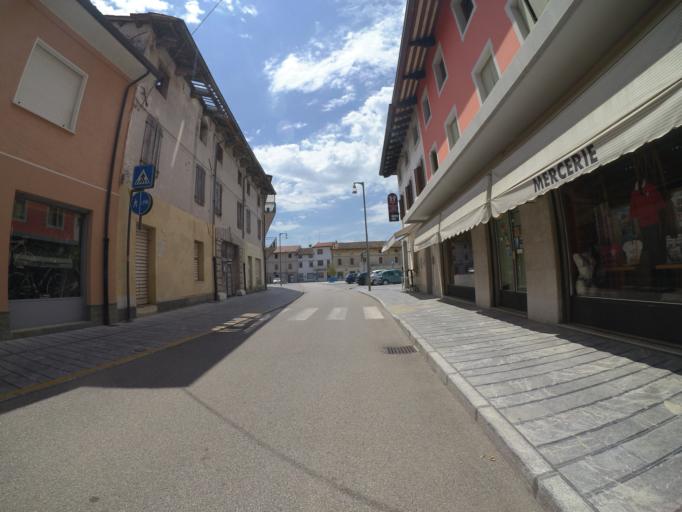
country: IT
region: Friuli Venezia Giulia
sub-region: Provincia di Udine
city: Talmassons
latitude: 45.9290
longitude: 13.1178
